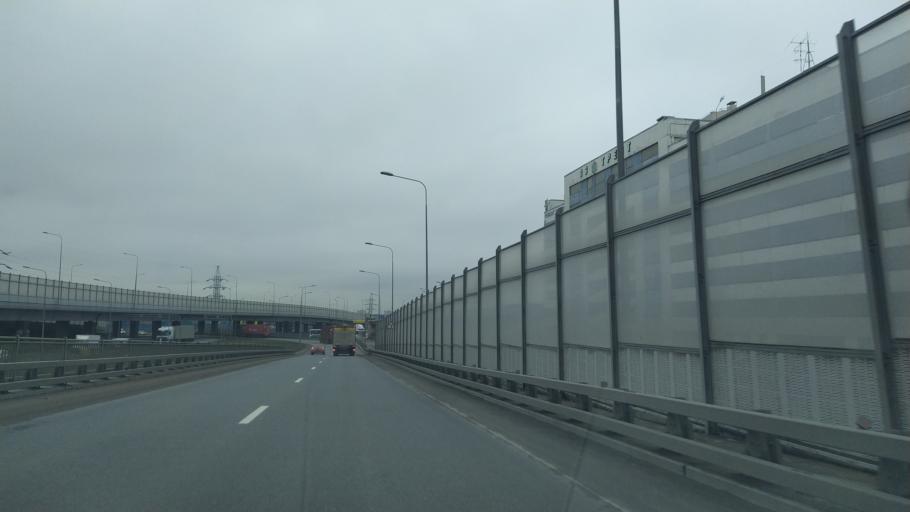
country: RU
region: St.-Petersburg
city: Kupchino
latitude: 59.8316
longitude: 30.3131
